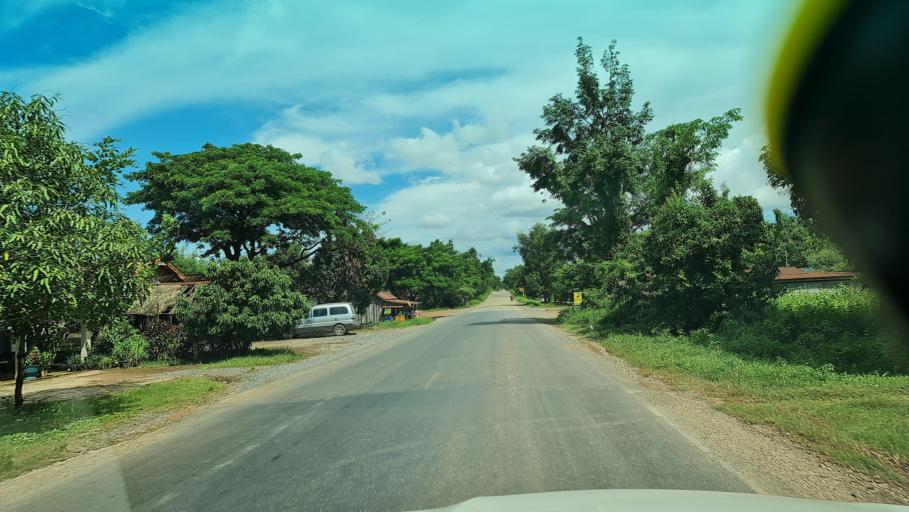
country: LA
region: Bolikhamxai
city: Ban Nahin
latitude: 18.2298
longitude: 104.1927
